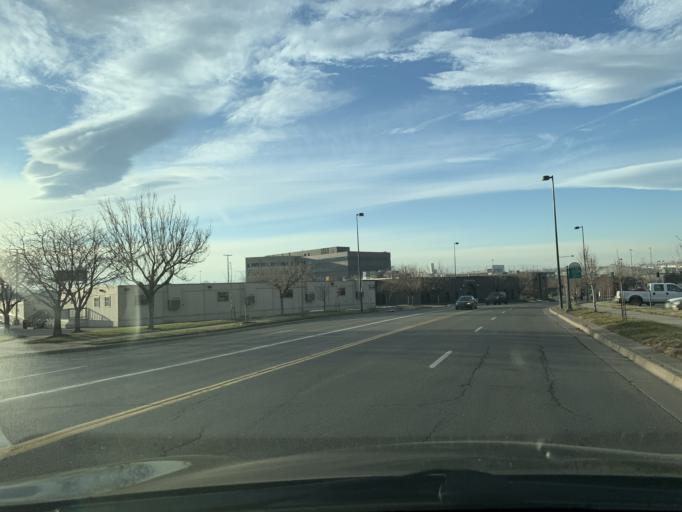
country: US
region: Colorado
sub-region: Denver County
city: Denver
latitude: 39.7414
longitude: -105.0062
